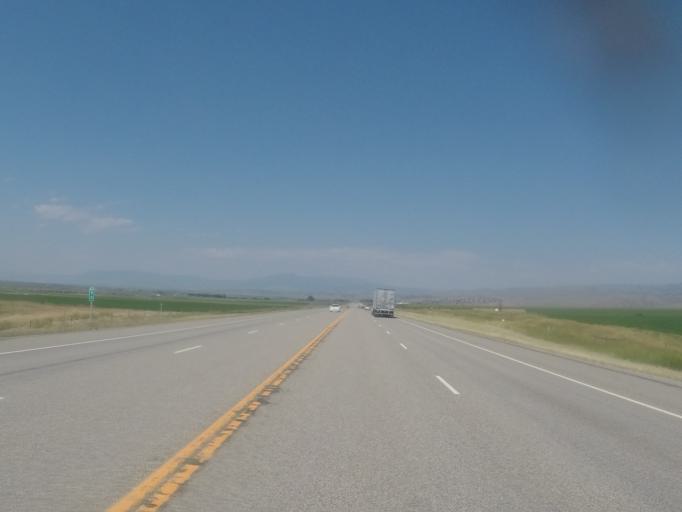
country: US
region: Montana
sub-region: Broadwater County
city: Townsend
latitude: 46.1164
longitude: -111.5017
